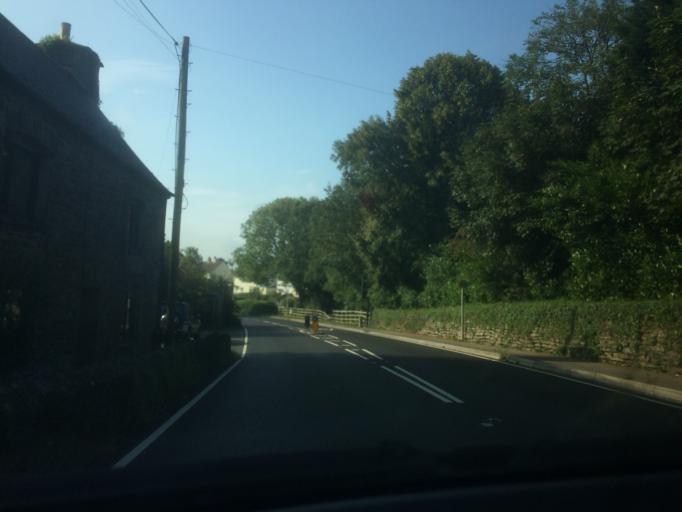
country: GB
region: England
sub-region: Cornwall
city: Pillaton
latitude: 50.4669
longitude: -4.2711
